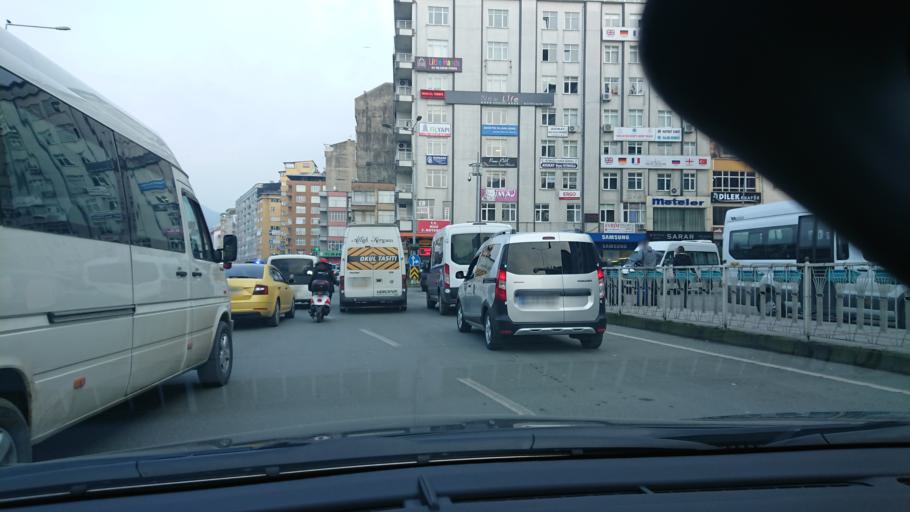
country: TR
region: Rize
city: Rize
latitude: 41.0260
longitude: 40.5199
